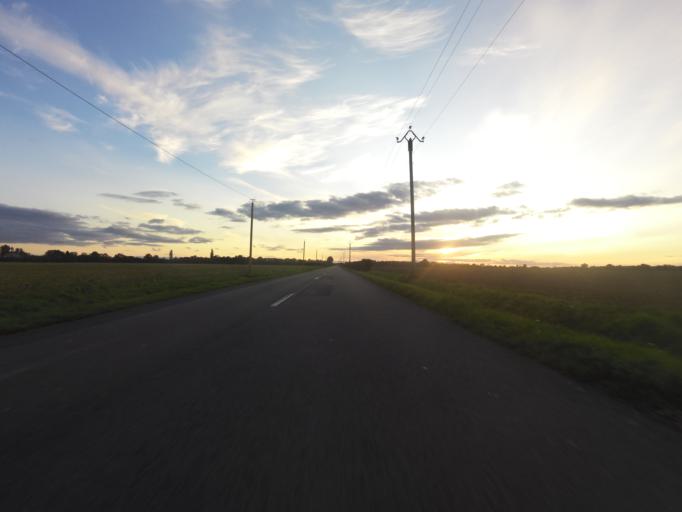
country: FR
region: Lower Normandy
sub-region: Departement du Calvados
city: La Vespiere
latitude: 48.9695
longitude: 0.3139
